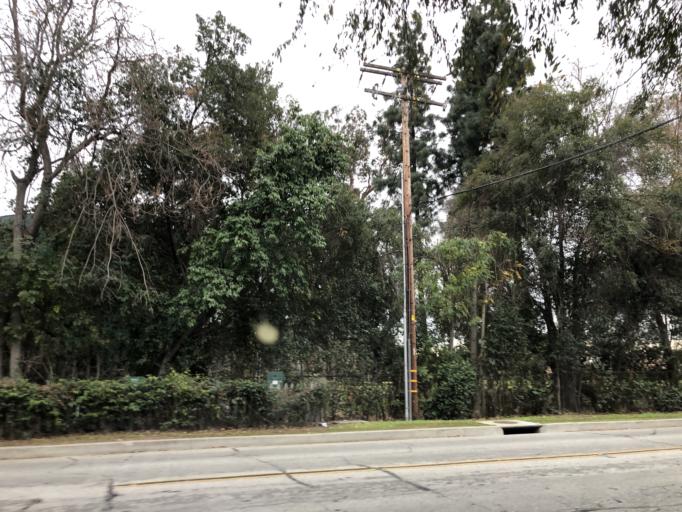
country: US
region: California
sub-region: Los Angeles County
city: San Marino
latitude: 34.1136
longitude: -118.0983
